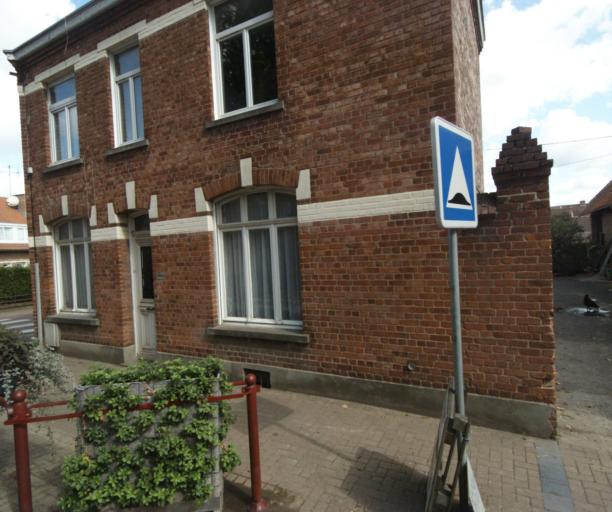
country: FR
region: Nord-Pas-de-Calais
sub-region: Departement du Nord
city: Sainghin-en-Melantois
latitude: 50.5873
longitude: 3.1626
